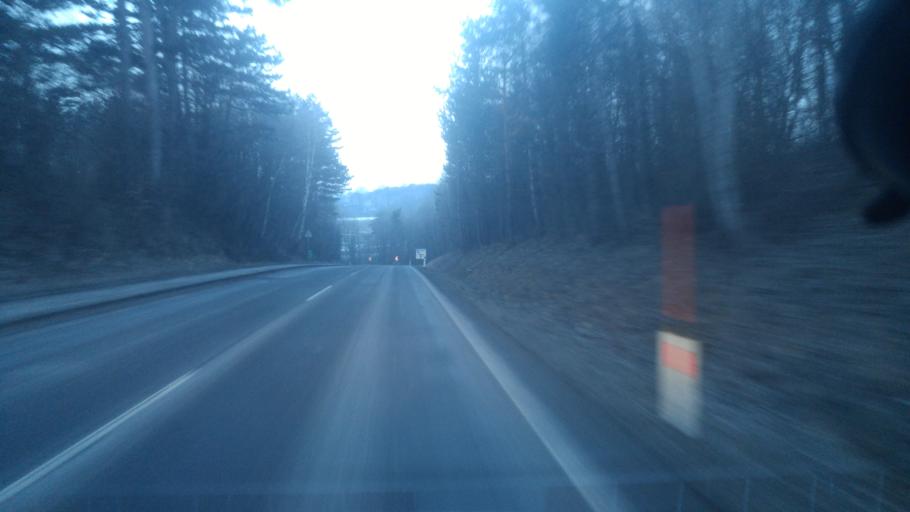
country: AT
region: Lower Austria
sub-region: Politischer Bezirk Baden
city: Berndorf
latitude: 47.9531
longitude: 16.1251
